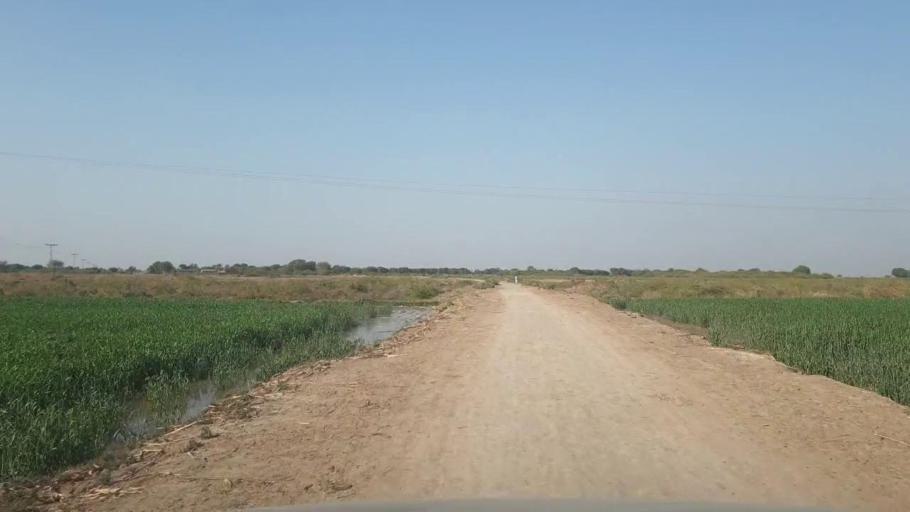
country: PK
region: Sindh
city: Chambar
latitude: 25.2981
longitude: 68.8630
